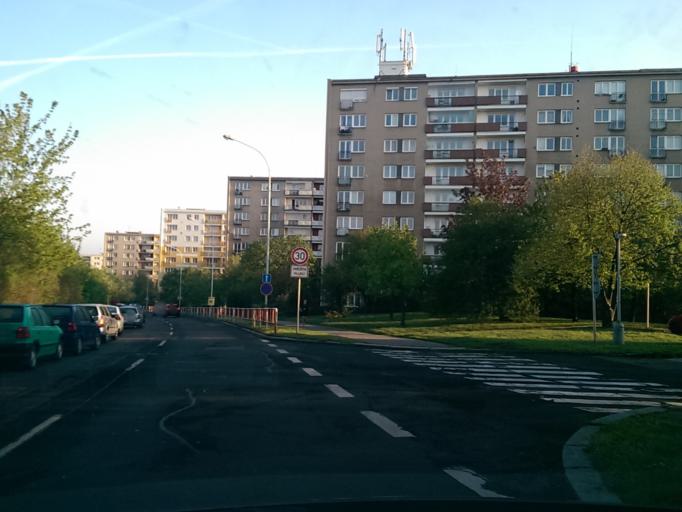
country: CZ
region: Praha
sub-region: Praha 8
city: Karlin
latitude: 50.0445
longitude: 14.4895
